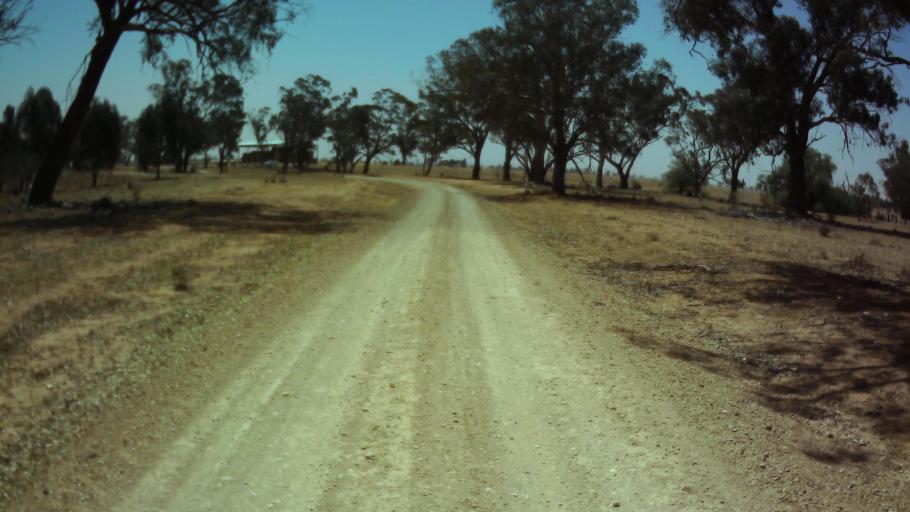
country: AU
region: New South Wales
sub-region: Weddin
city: Grenfell
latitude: -34.0151
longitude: 147.8972
